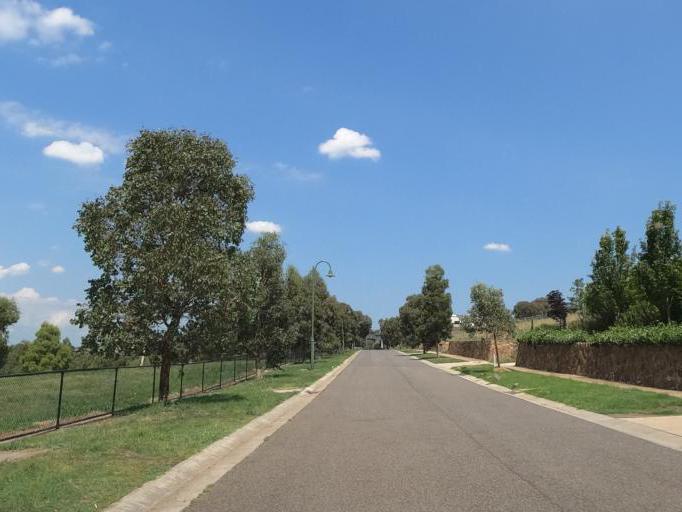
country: AU
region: Victoria
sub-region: Hume
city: Meadow Heights
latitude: -37.6398
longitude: 144.9003
